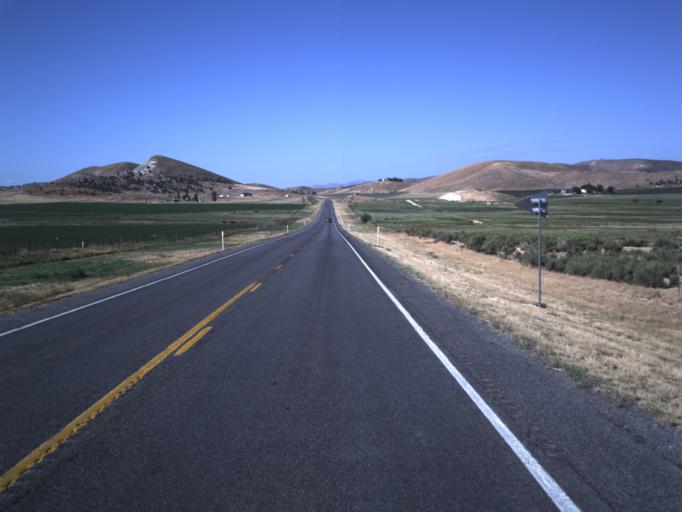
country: US
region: Utah
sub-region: Sanpete County
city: Manti
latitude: 39.2266
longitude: -111.6726
